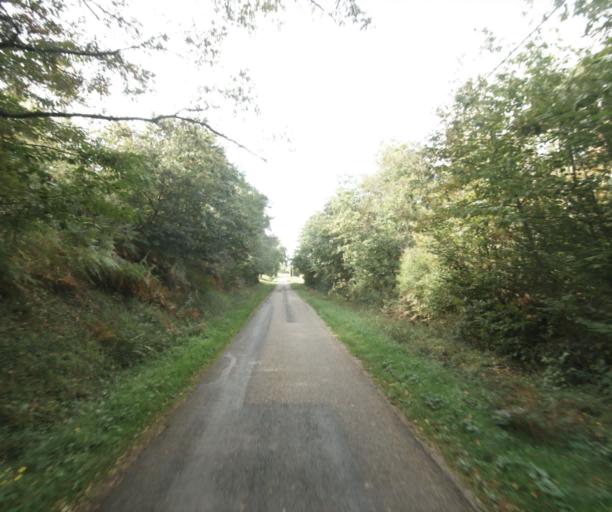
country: FR
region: Midi-Pyrenees
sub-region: Departement du Gers
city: Le Houga
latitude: 43.8623
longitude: -0.1367
